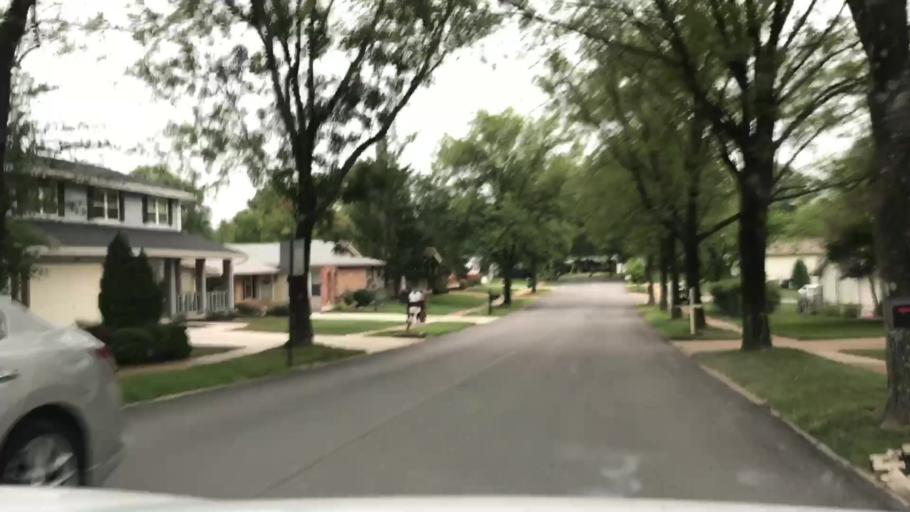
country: US
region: Missouri
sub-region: Saint Louis County
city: Ballwin
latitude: 38.5825
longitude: -90.5629
